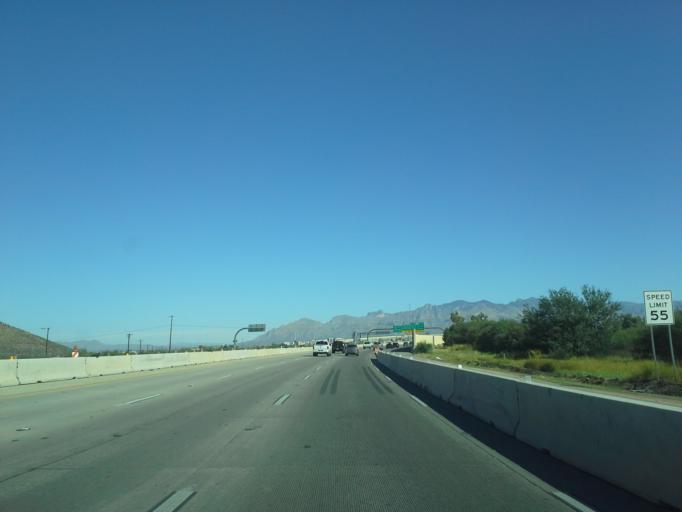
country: US
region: Arizona
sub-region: Pima County
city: South Tucson
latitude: 32.1829
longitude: -110.9851
